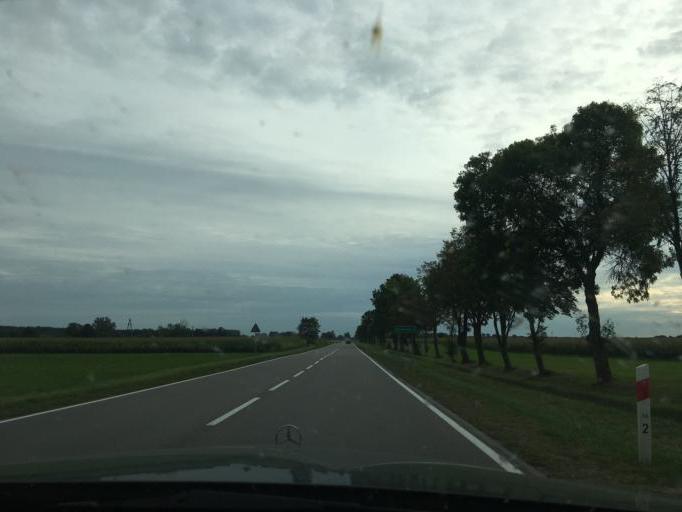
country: PL
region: Masovian Voivodeship
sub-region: Powiat ostrowski
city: Ostrow Mazowiecka
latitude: 52.8905
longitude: 21.8668
